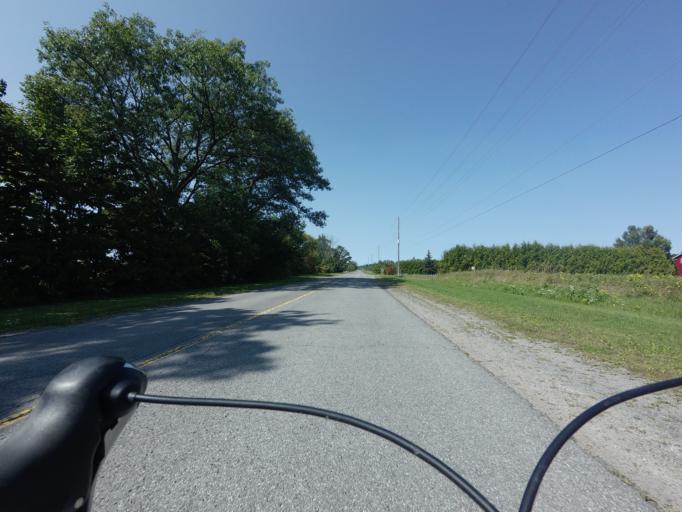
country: CA
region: Ontario
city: Arnprior
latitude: 45.4857
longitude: -76.1297
